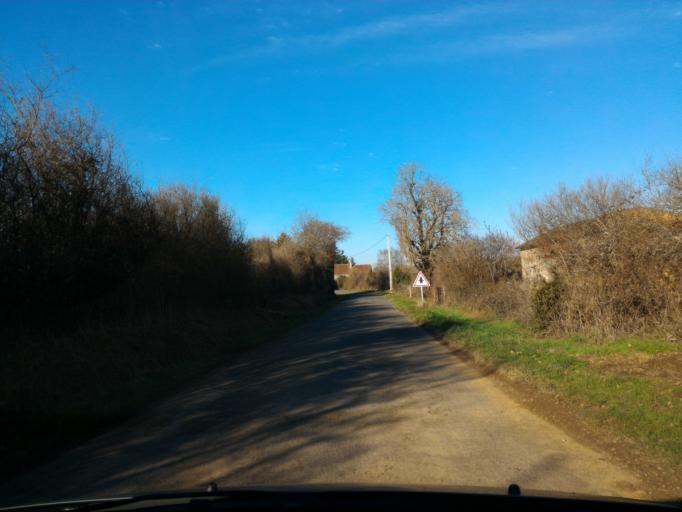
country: FR
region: Poitou-Charentes
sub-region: Departement de la Charente
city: Nanteuil-en-Vallee
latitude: 45.9547
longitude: 0.3570
